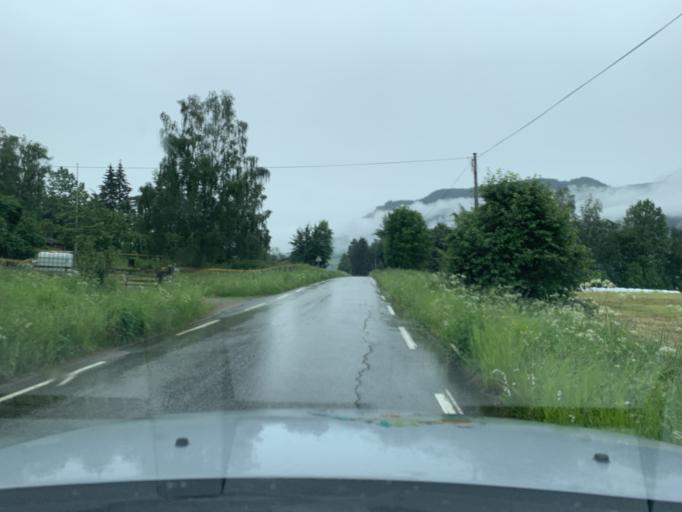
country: NO
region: Oppland
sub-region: Oyer
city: Tretten
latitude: 61.3932
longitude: 10.2405
